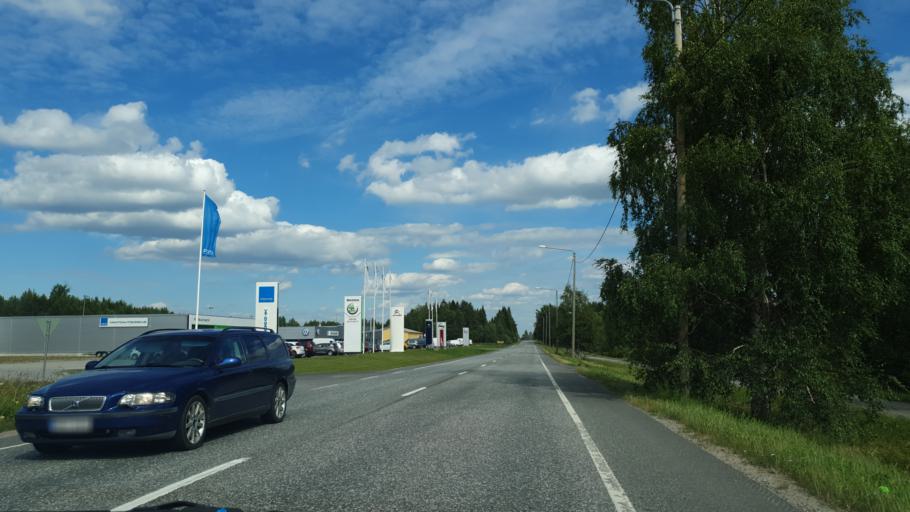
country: FI
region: Kainuu
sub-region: Kajaani
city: Kajaani
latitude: 64.2496
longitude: 27.7771
